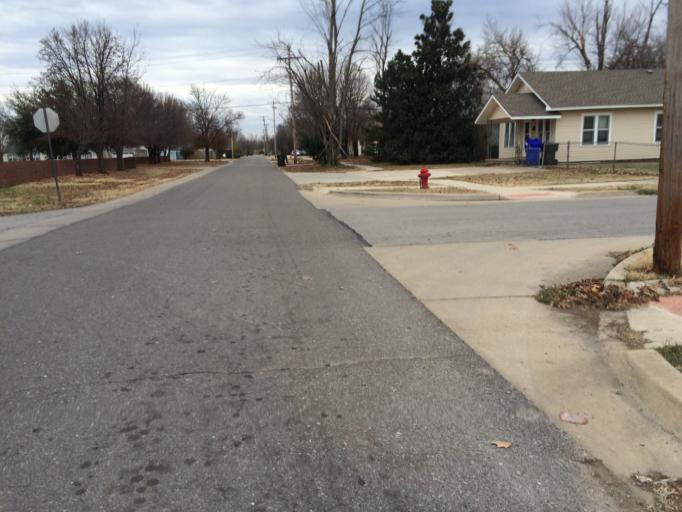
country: US
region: Oklahoma
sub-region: Cleveland County
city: Norman
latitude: 35.2298
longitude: -97.4427
